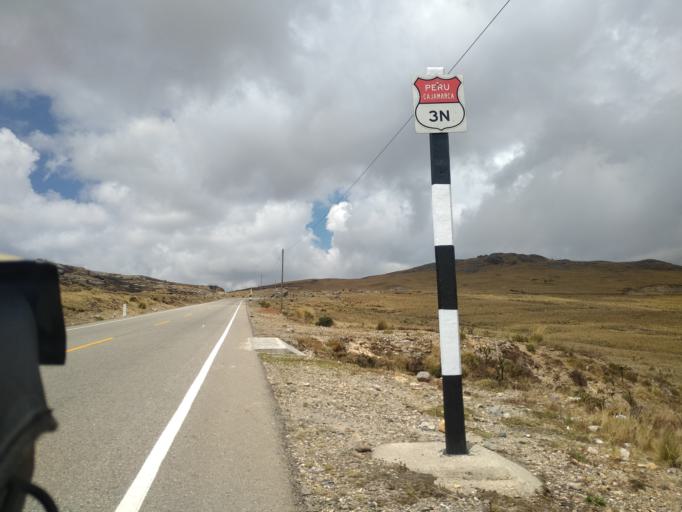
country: PE
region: La Libertad
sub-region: Provincia de Santiago de Chuco
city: Quiruvilca
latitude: -7.9475
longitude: -78.1907
